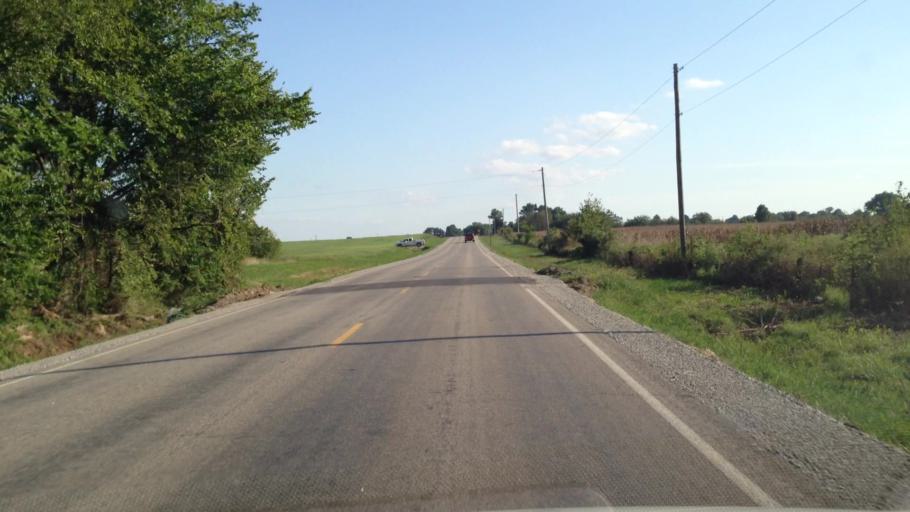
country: US
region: Kansas
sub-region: Crawford County
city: Pittsburg
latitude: 37.3448
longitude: -94.6316
